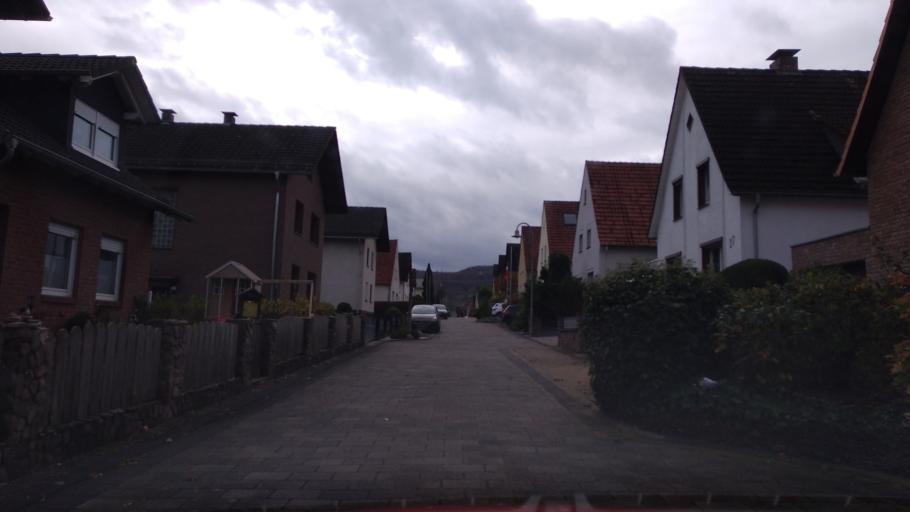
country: DE
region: North Rhine-Westphalia
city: Beverungen
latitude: 51.6665
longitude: 9.3702
